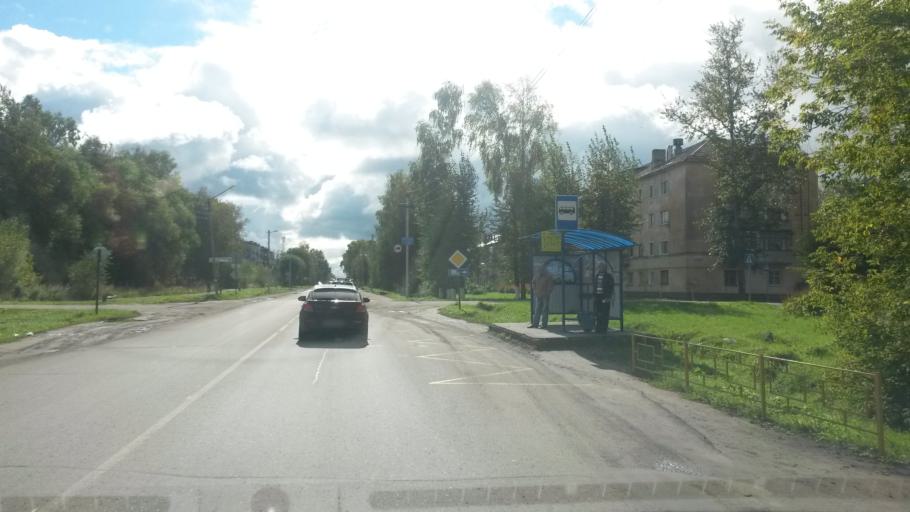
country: RU
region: Ivanovo
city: Zavolzhsk
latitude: 57.4951
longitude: 42.1339
